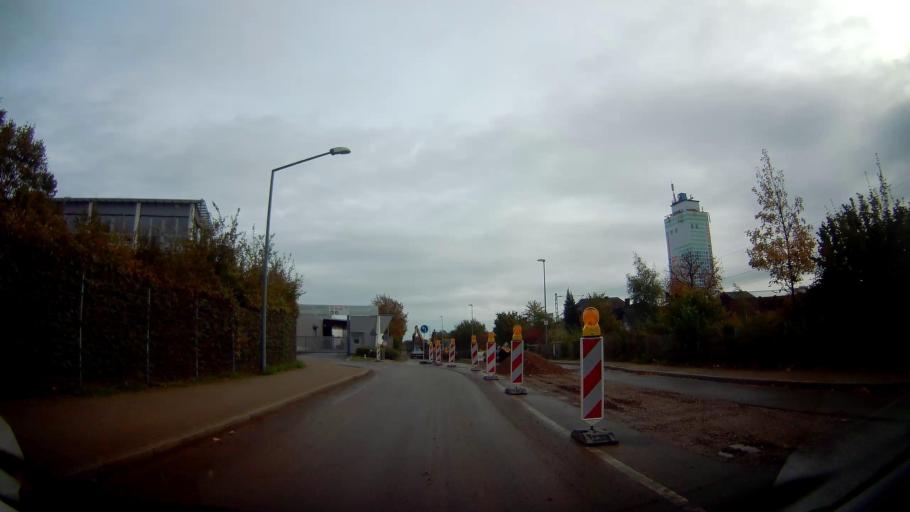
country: DE
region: North Rhine-Westphalia
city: Herten
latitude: 51.5959
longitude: 7.1308
